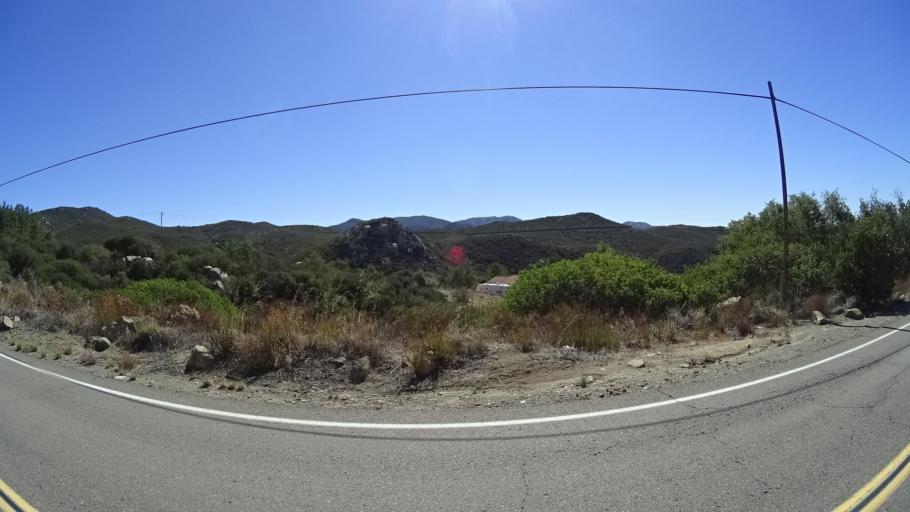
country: US
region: California
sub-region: San Diego County
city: Descanso
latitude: 32.8051
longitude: -116.6404
